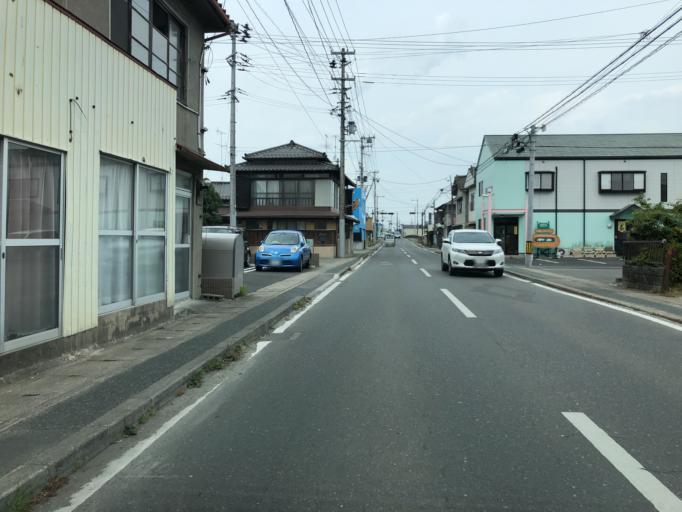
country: JP
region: Miyagi
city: Marumori
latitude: 37.7945
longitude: 140.9244
